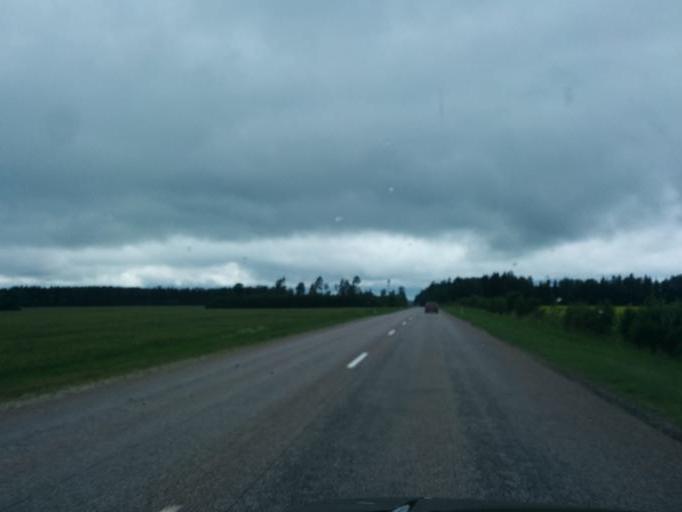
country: LV
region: Beverina
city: Murmuiza
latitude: 57.4858
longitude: 25.5959
